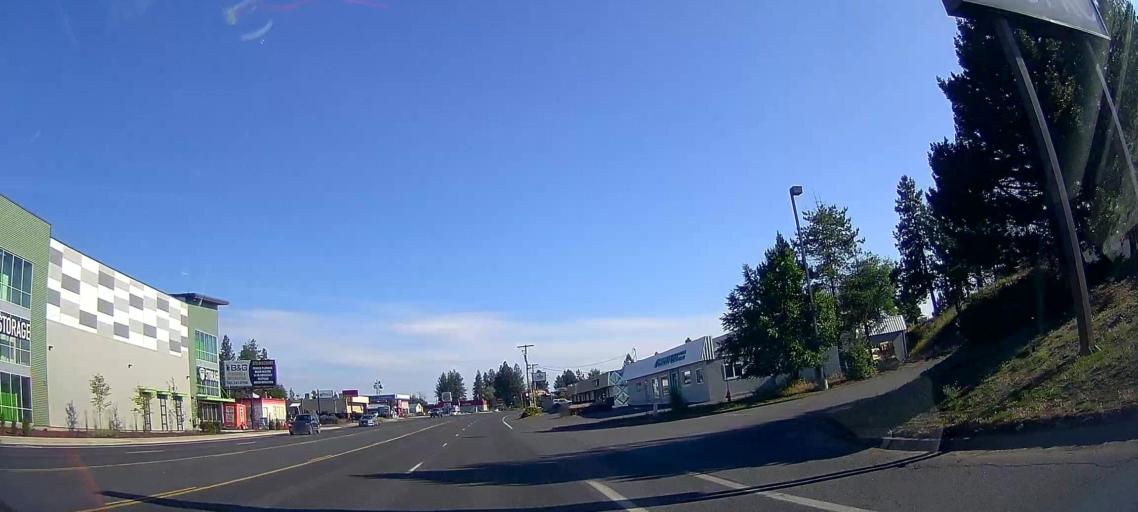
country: US
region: Oregon
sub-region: Deschutes County
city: Bend
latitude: 44.0848
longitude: -121.3058
